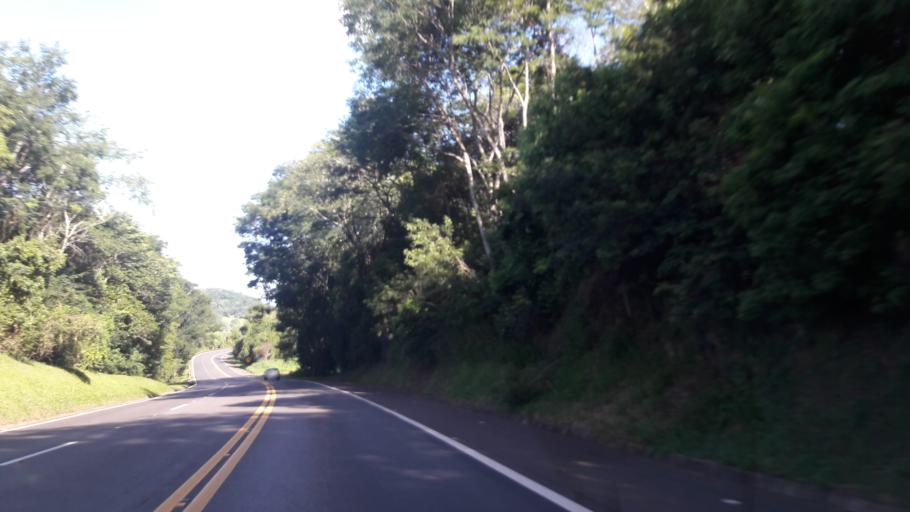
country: BR
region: Parana
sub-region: Laranjeiras Do Sul
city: Laranjeiras do Sul
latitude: -25.4122
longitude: -52.0857
